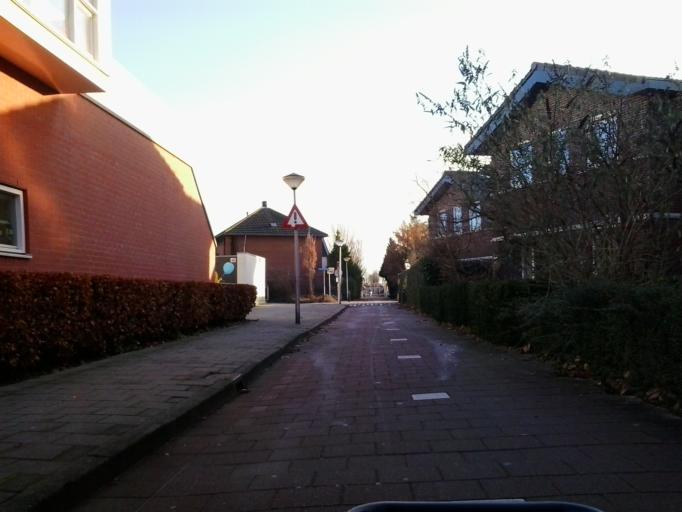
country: NL
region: South Holland
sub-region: Gemeente Lansingerland
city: Bergschenhoek
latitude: 51.9931
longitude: 4.5048
